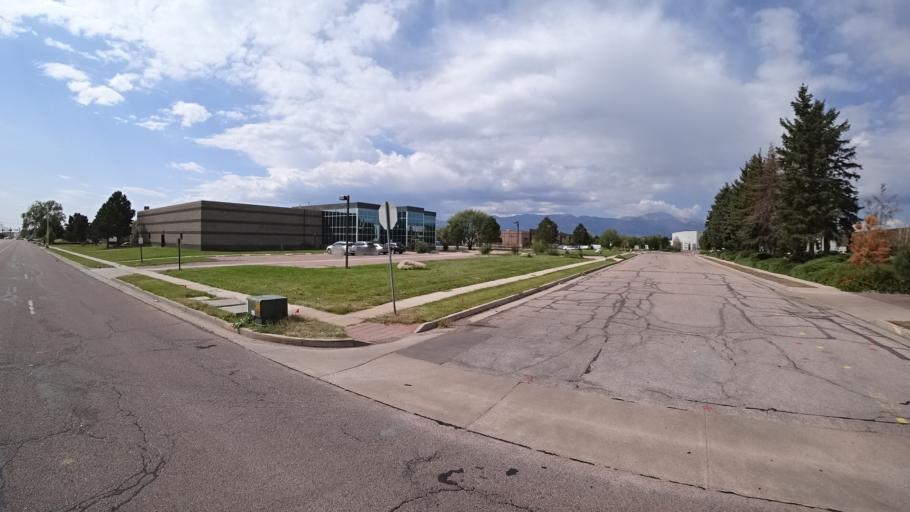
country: US
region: Colorado
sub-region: El Paso County
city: Cimarron Hills
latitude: 38.8428
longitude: -104.7388
